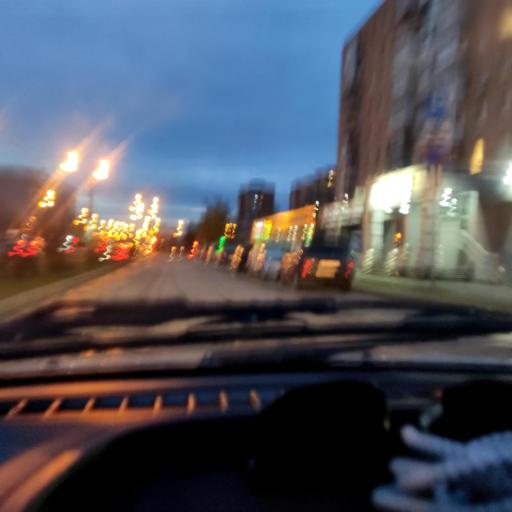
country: RU
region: Samara
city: Zhigulevsk
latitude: 53.4834
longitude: 49.4861
